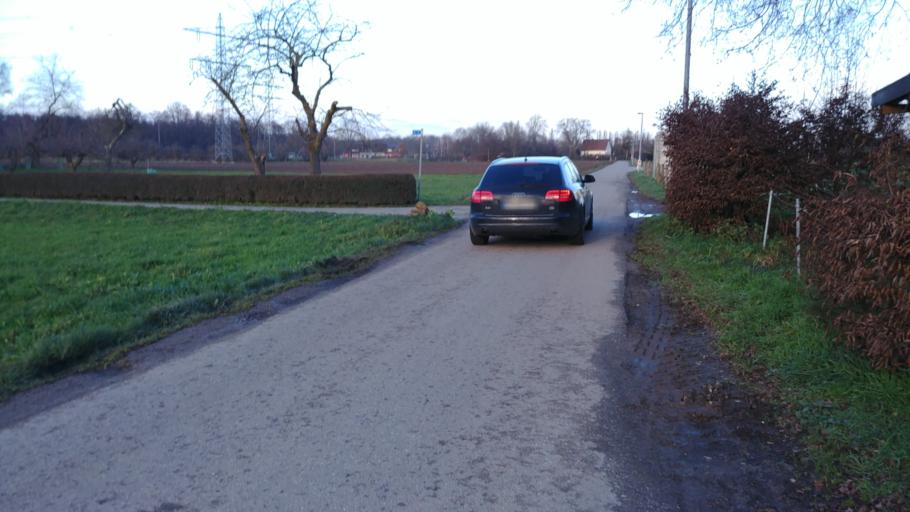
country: DE
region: Baden-Wuerttemberg
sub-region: Karlsruhe Region
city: Ettlingen
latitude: 48.9655
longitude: 8.3893
